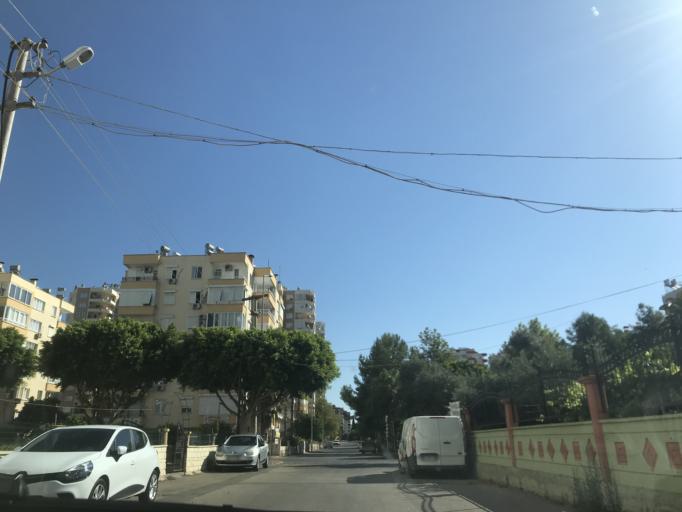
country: TR
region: Antalya
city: Antalya
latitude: 36.8934
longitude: 30.6298
